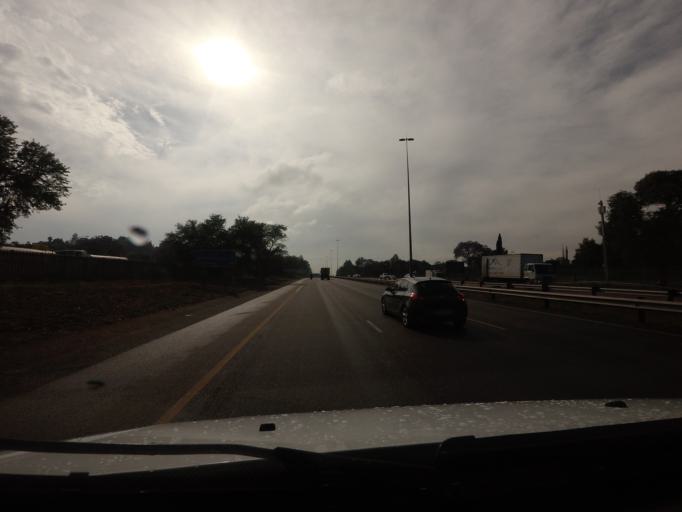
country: ZA
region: Gauteng
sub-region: City of Tshwane Metropolitan Municipality
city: Pretoria
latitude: -25.7409
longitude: 28.2805
